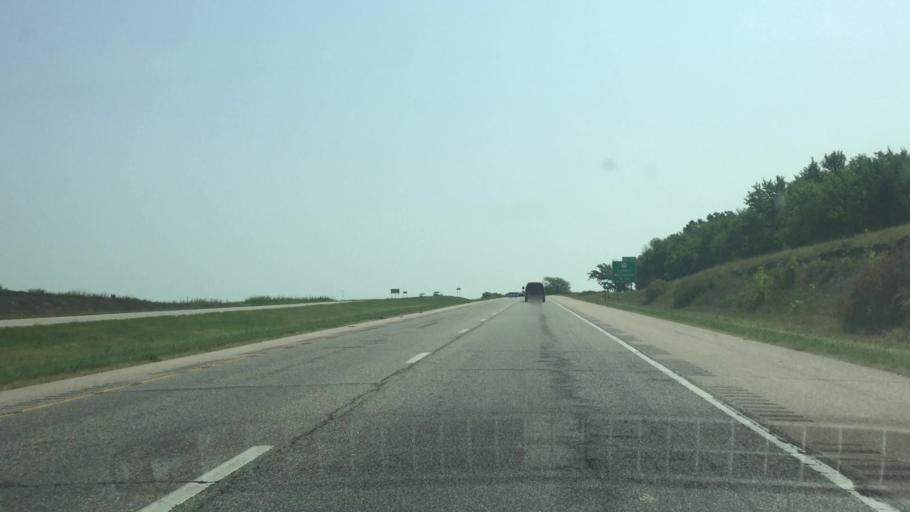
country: US
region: Kansas
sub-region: Osage County
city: Lyndon
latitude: 38.4260
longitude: -95.7463
